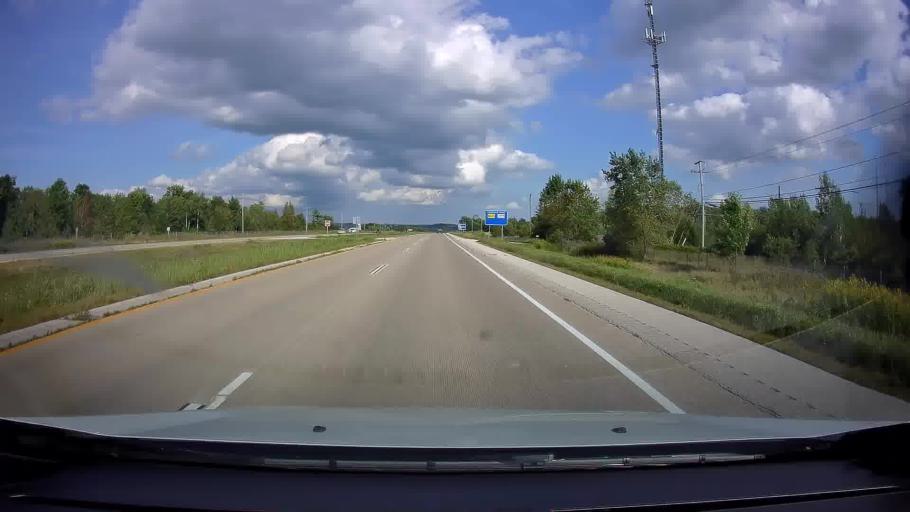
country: US
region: Wisconsin
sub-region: Kewaunee County
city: Luxemburg
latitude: 44.6336
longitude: -87.7922
